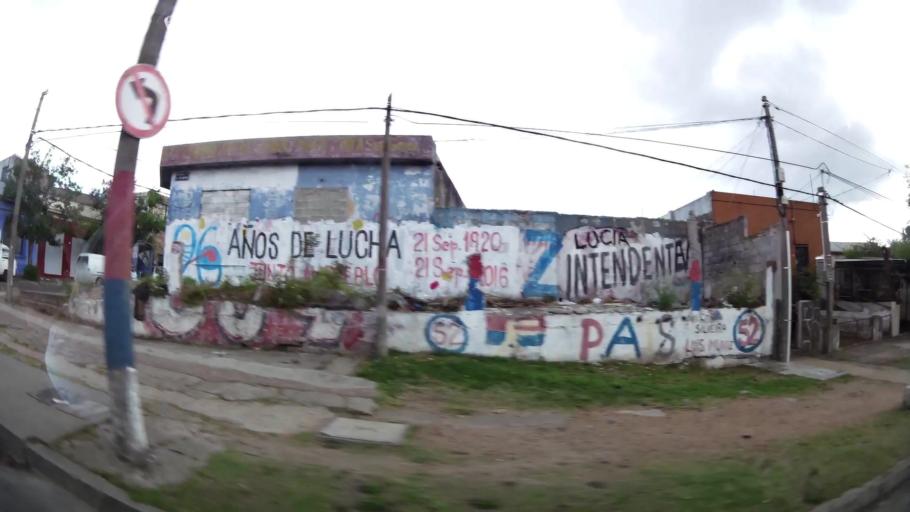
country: UY
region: Montevideo
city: Montevideo
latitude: -34.8480
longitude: -56.1701
